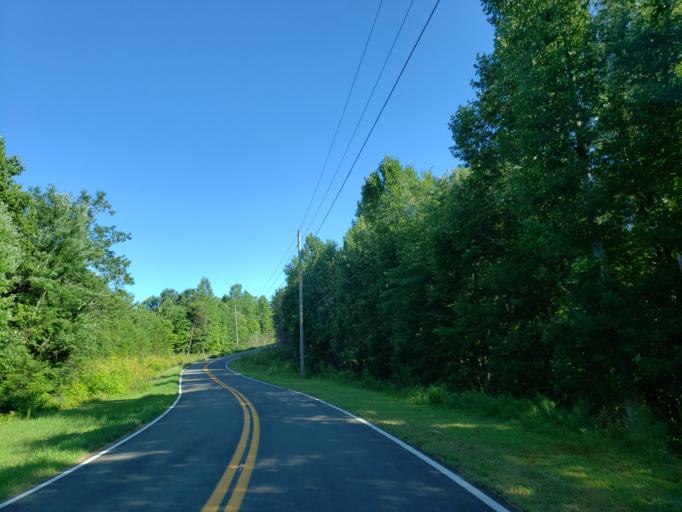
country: US
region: Georgia
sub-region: Bartow County
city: Rydal
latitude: 34.3651
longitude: -84.6200
